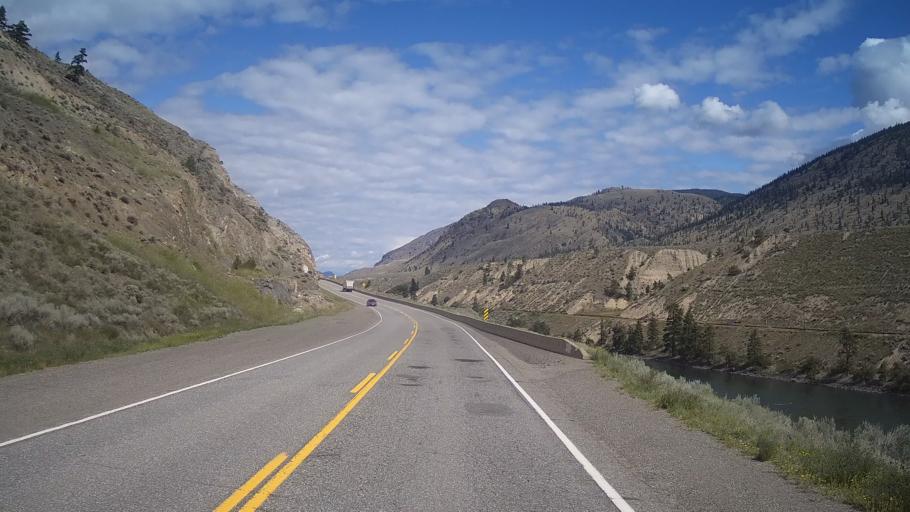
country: CA
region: British Columbia
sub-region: Thompson-Nicola Regional District
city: Ashcroft
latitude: 50.5333
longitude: -121.2857
